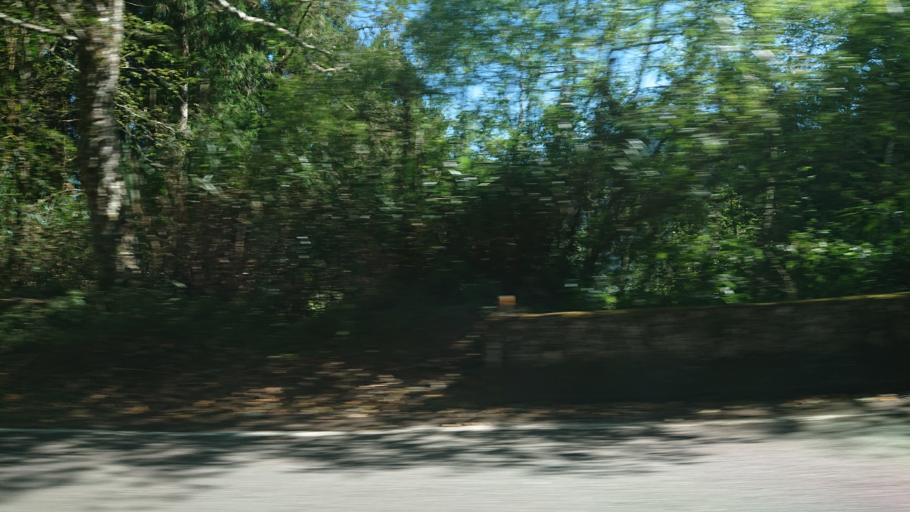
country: TW
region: Taiwan
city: Lugu
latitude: 23.4805
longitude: 120.8328
